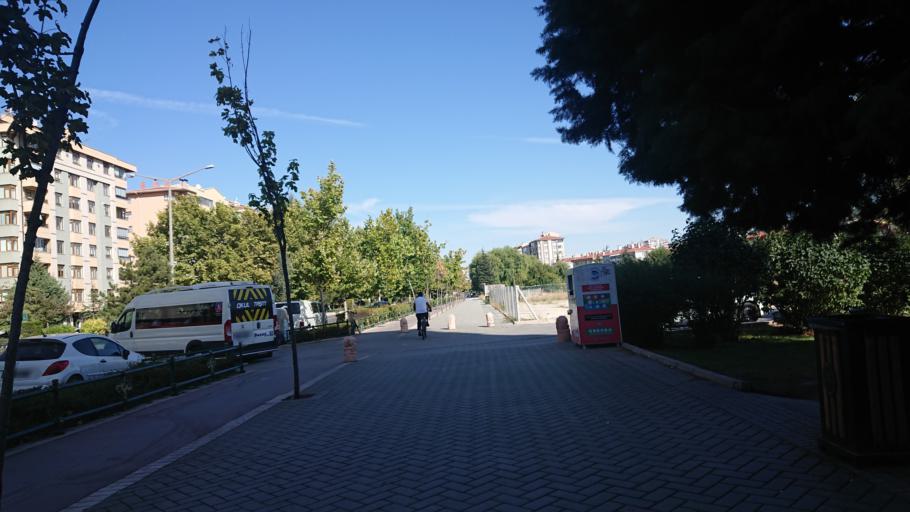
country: TR
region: Eskisehir
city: Eskisehir
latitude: 39.7647
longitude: 30.5059
